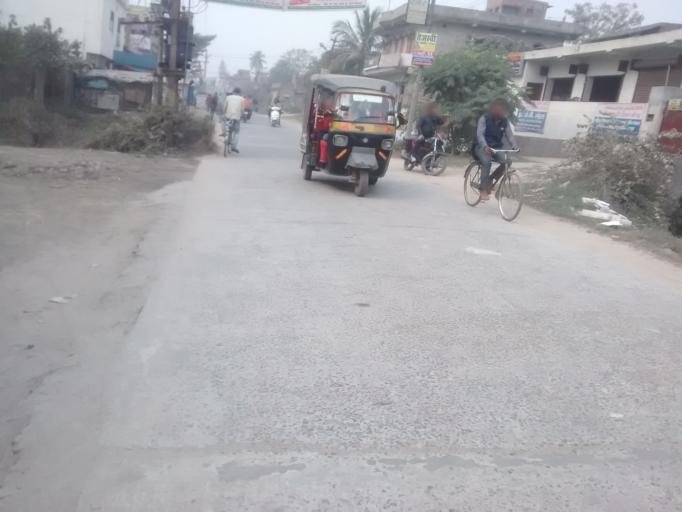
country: IN
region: Bihar
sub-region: Muzaffarpur
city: Muzaffarpur
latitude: 26.1026
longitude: 85.4049
